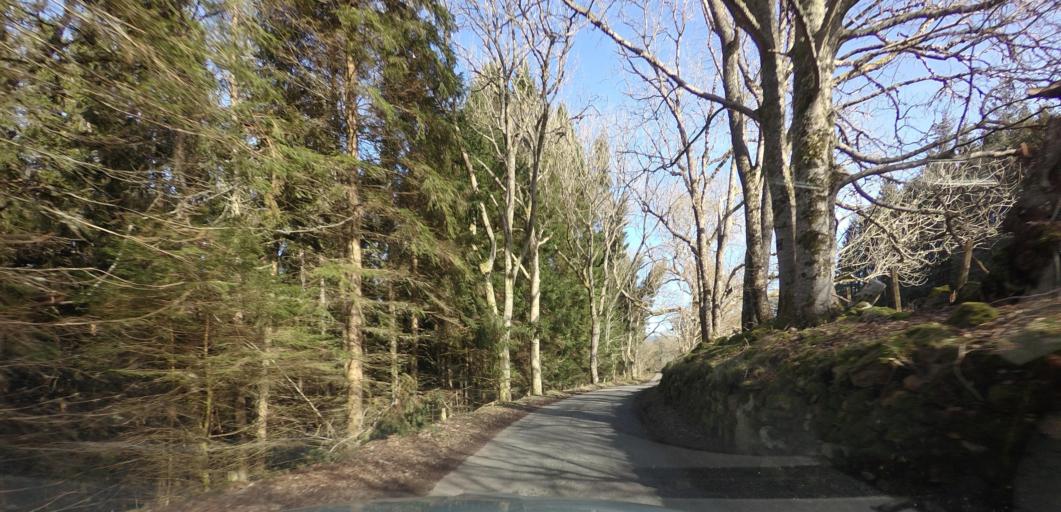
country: GB
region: Scotland
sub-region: Perth and Kinross
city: Comrie
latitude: 56.5485
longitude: -4.0964
